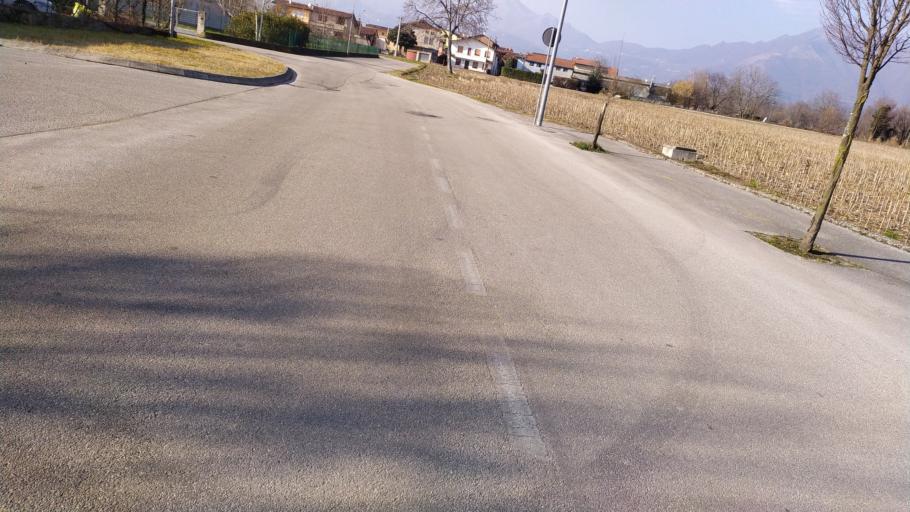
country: IT
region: Veneto
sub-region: Provincia di Vicenza
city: Giavenale
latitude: 45.6875
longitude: 11.4020
